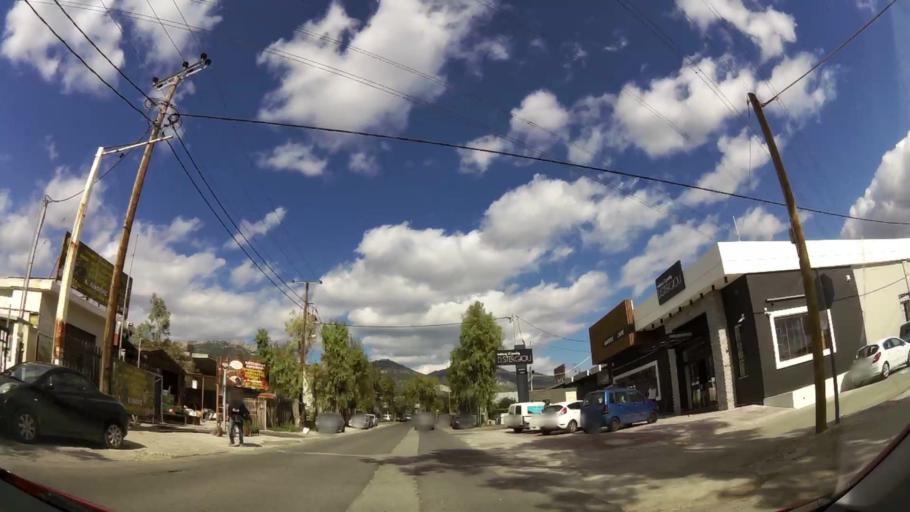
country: GR
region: Attica
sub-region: Nomarchia Anatolikis Attikis
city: Acharnes
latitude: 38.1058
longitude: 23.7430
